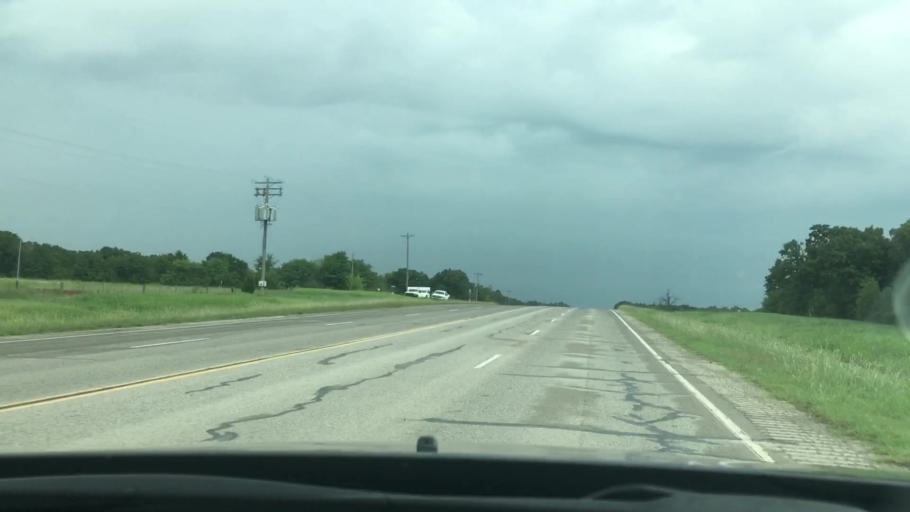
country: US
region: Oklahoma
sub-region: Carter County
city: Healdton
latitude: 34.1859
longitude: -97.4747
